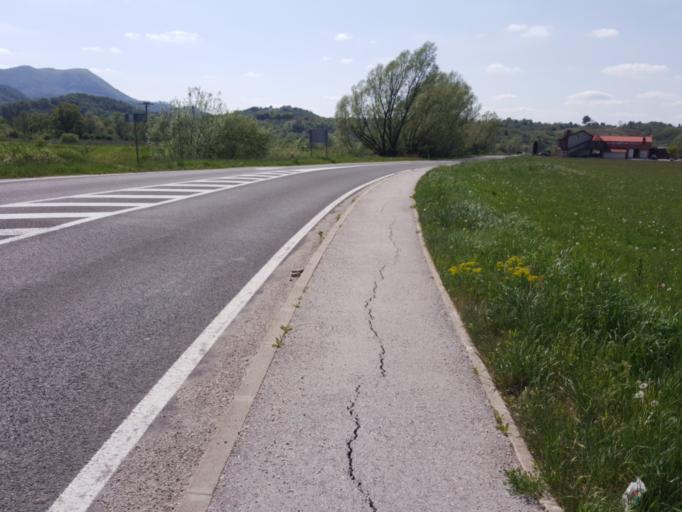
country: HR
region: Varazdinska
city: Lepoglava
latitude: 46.2261
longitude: 15.9778
